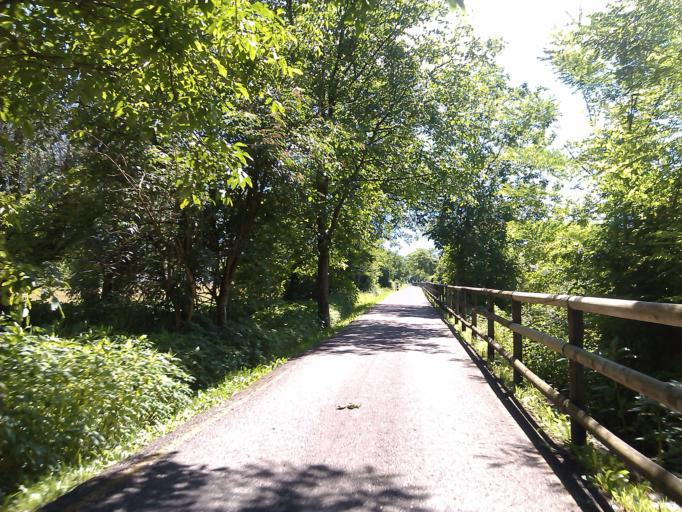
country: IT
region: Trentino-Alto Adige
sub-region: Provincia di Trento
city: Castelnuovo
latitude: 46.0486
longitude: 11.4988
